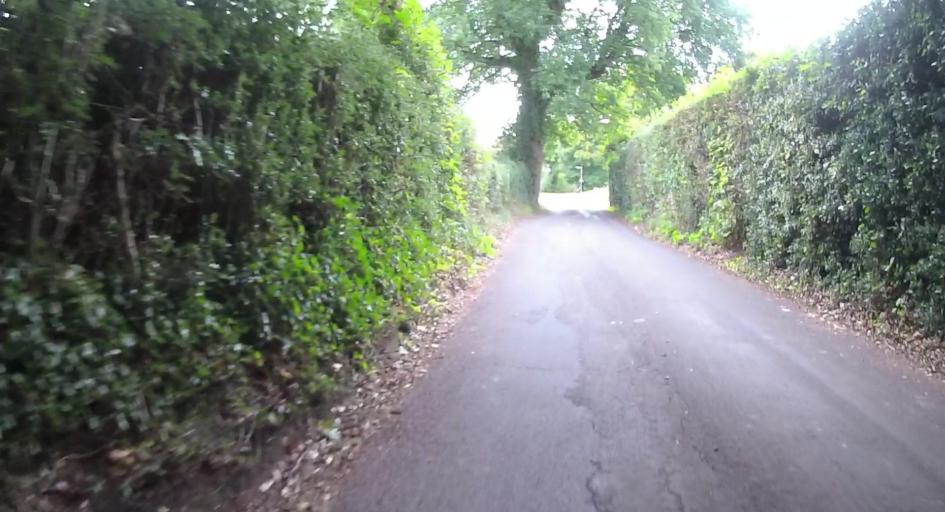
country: GB
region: England
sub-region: Surrey
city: Knaphill
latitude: 51.3258
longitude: -0.6304
